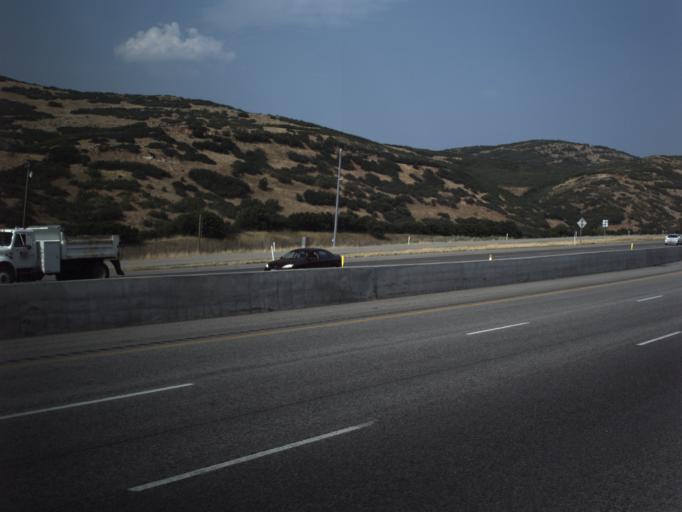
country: US
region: Utah
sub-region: Summit County
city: Summit Park
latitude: 40.7393
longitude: -111.6678
